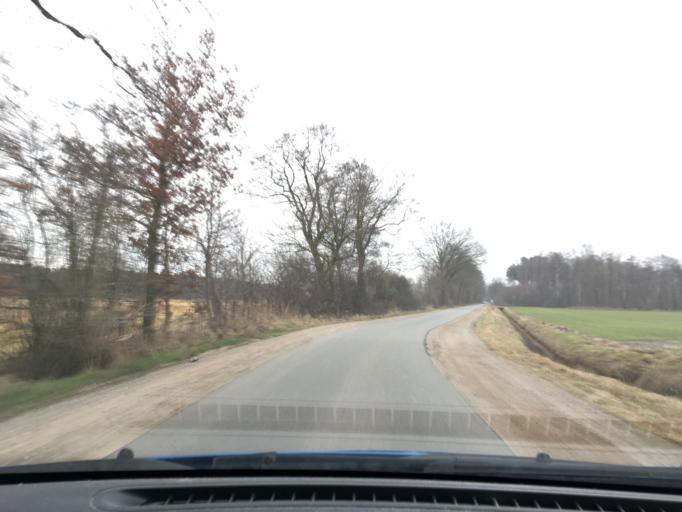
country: DE
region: Lower Saxony
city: Vogelsen
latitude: 53.2958
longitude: 10.3354
